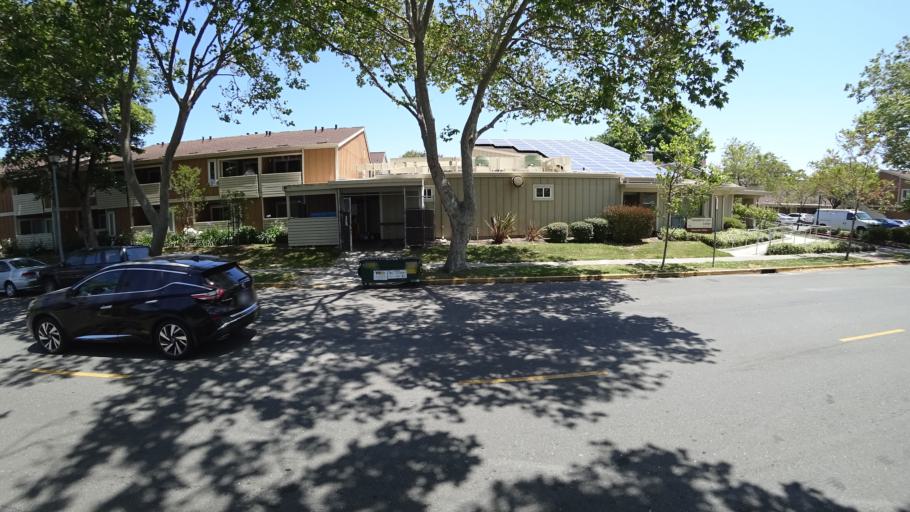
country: US
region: California
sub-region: Alameda County
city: Hayward
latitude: 37.6287
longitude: -122.1001
